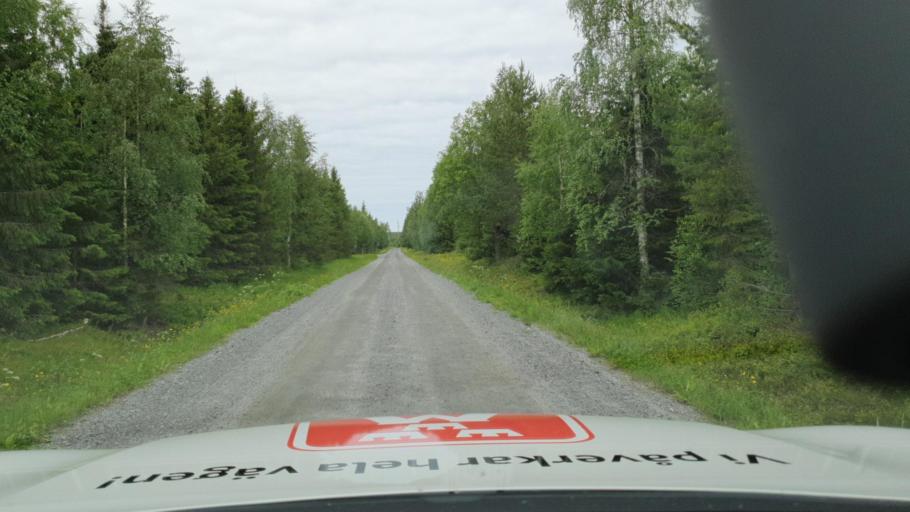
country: SE
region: Vaesterbotten
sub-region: Skelleftea Kommun
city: Burtraesk
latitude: 64.4457
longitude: 20.3524
